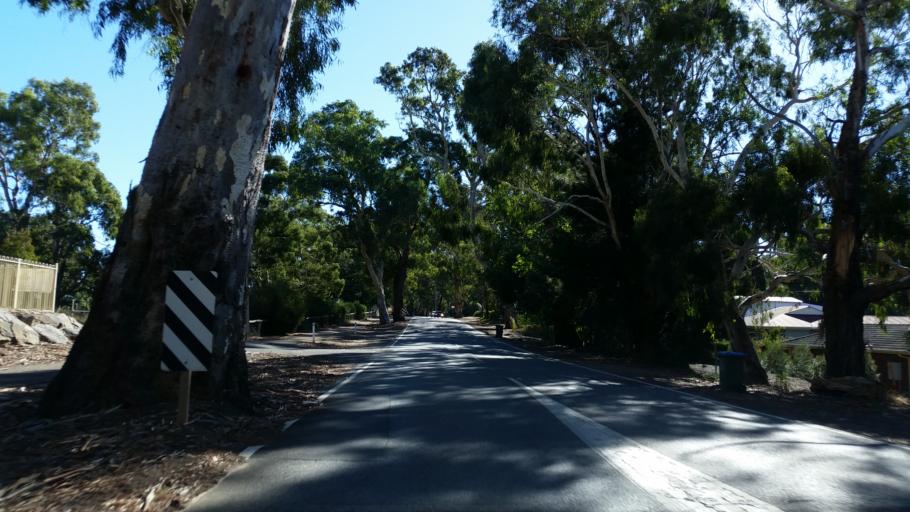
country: AU
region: South Australia
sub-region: Adelaide Hills
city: Birdwood
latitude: -34.8205
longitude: 138.9524
